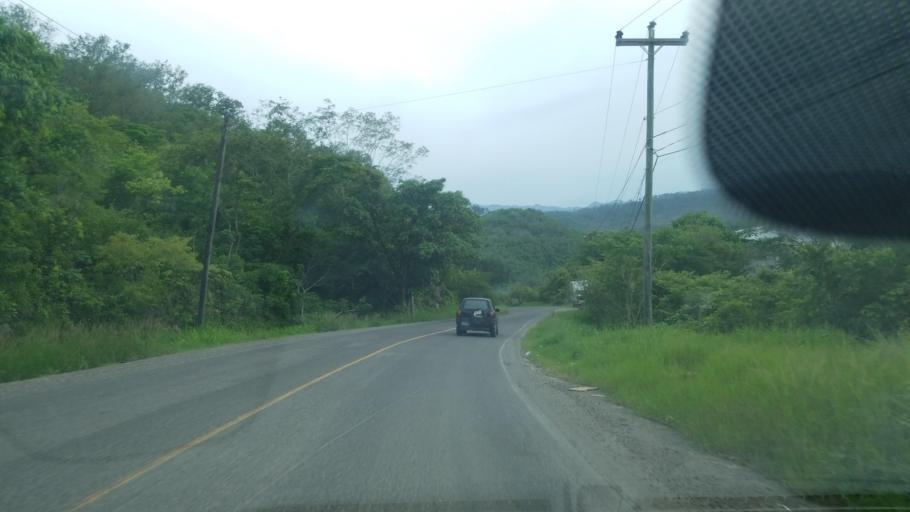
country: HN
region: Santa Barbara
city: Santa Barbara
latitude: 14.9173
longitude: -88.2501
